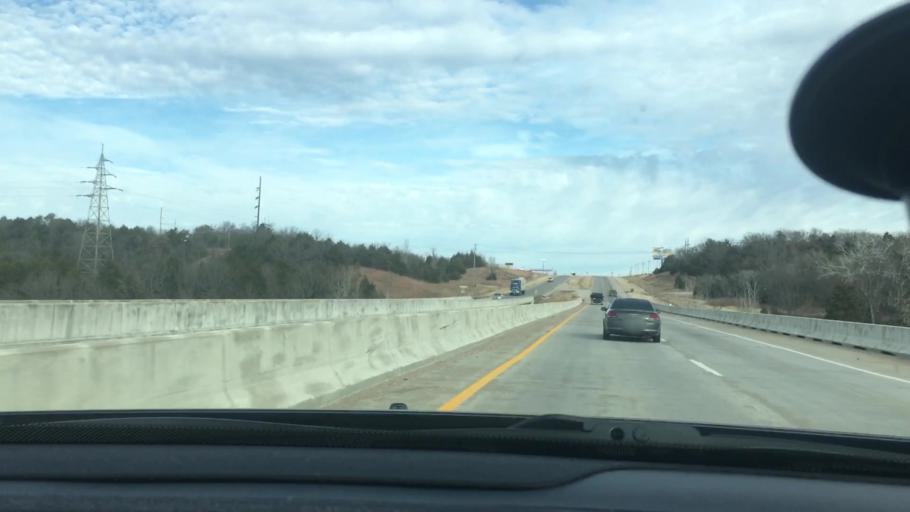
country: US
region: Oklahoma
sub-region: Pontotoc County
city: Byng
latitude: 34.9328
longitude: -96.6834
